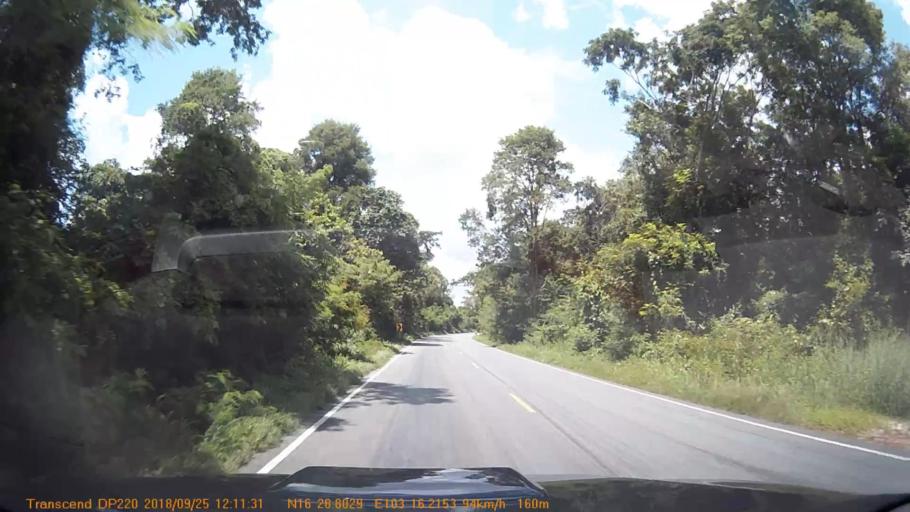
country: TH
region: Kalasin
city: Huai Mek
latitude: 16.4802
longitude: 103.2702
